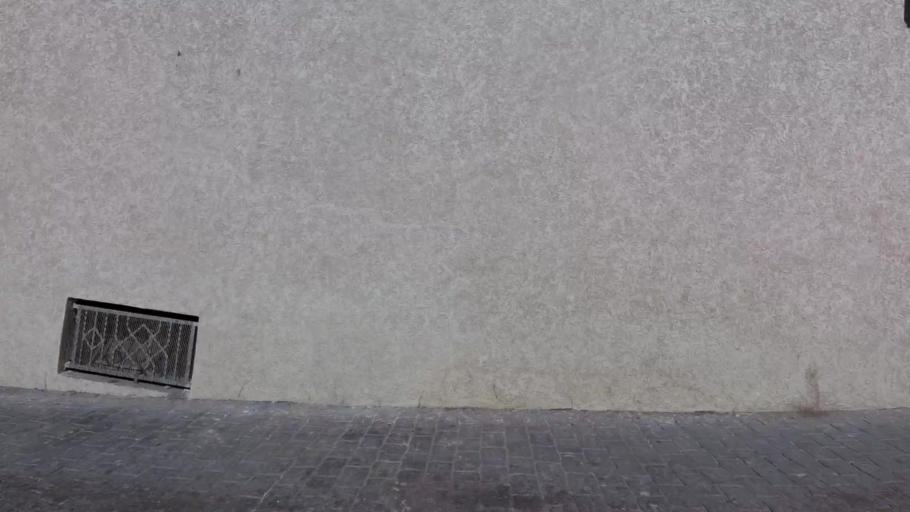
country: MA
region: Tanger-Tetouan
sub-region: Tanger-Assilah
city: Tangier
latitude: 35.7491
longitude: -5.8055
